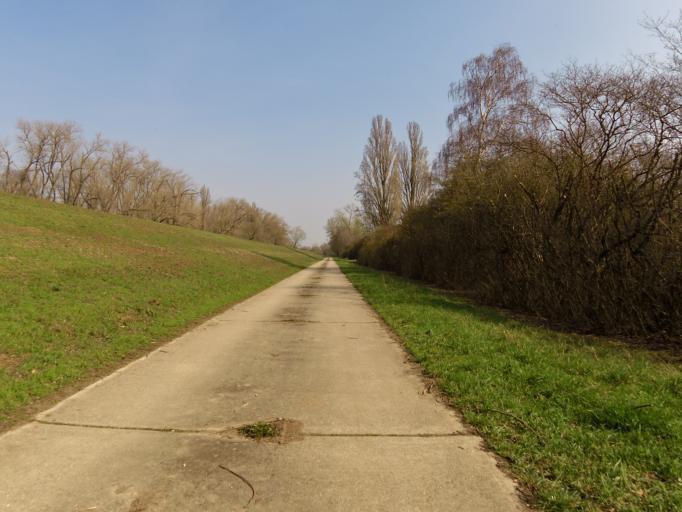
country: DE
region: Hesse
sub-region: Regierungsbezirk Darmstadt
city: Biblis
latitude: 49.7128
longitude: 8.4321
